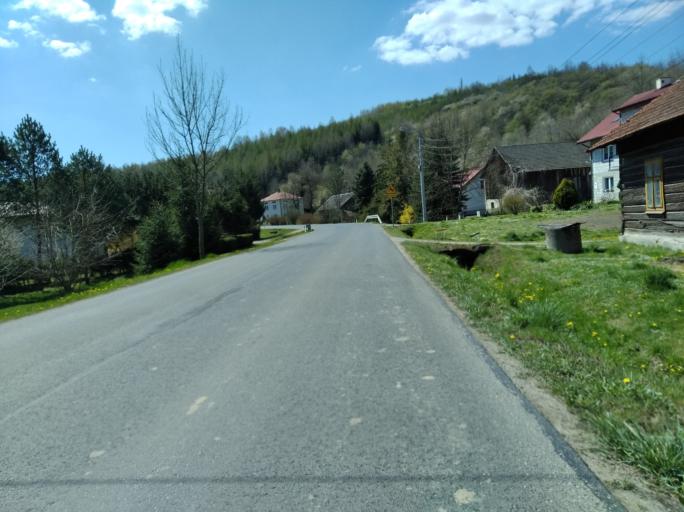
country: PL
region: Subcarpathian Voivodeship
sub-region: Powiat brzozowski
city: Dydnia
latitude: 49.6937
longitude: 22.1849
